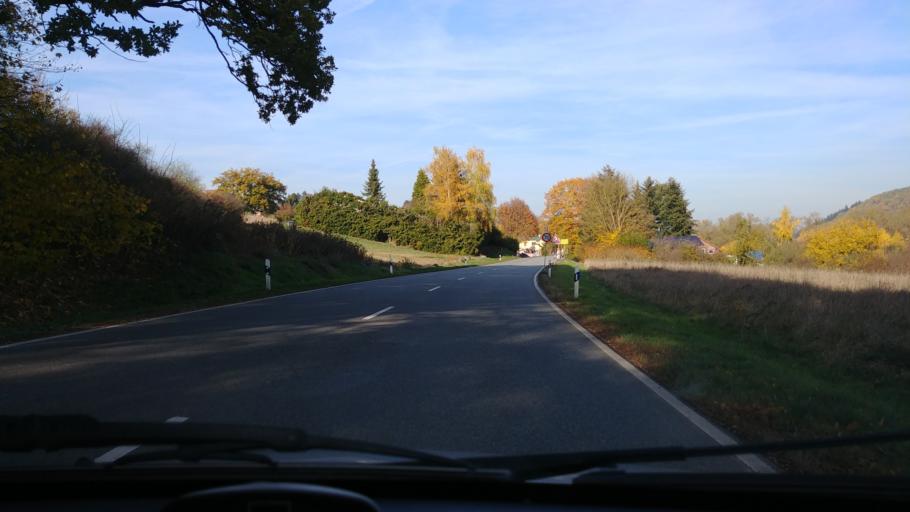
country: DE
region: Rheinland-Pfalz
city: Schiesheim
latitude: 50.2598
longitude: 8.0535
